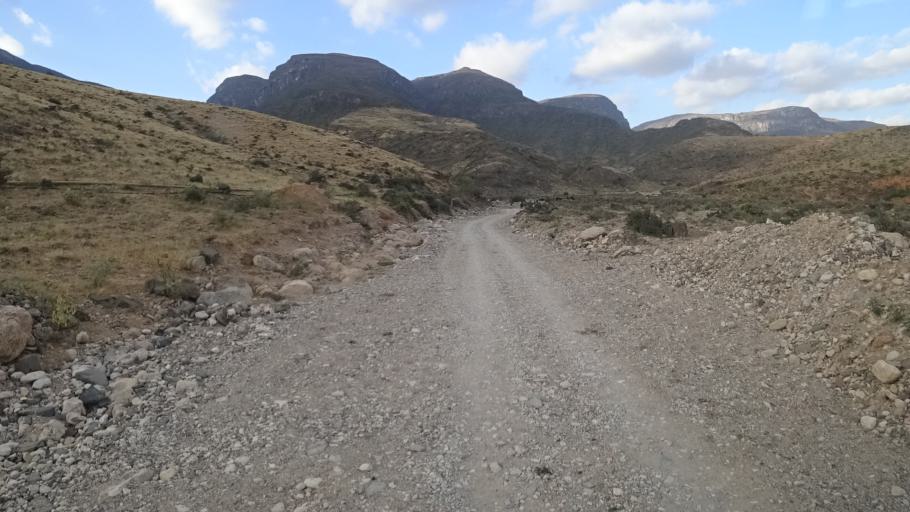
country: OM
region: Zufar
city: Salalah
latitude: 16.9938
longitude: 53.8459
